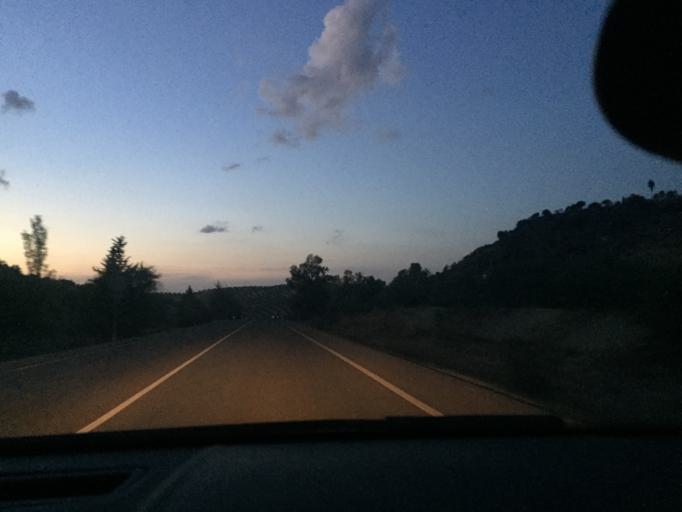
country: ES
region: Andalusia
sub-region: Provincia de Jaen
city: Mancha Real
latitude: 37.8001
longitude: -3.6658
